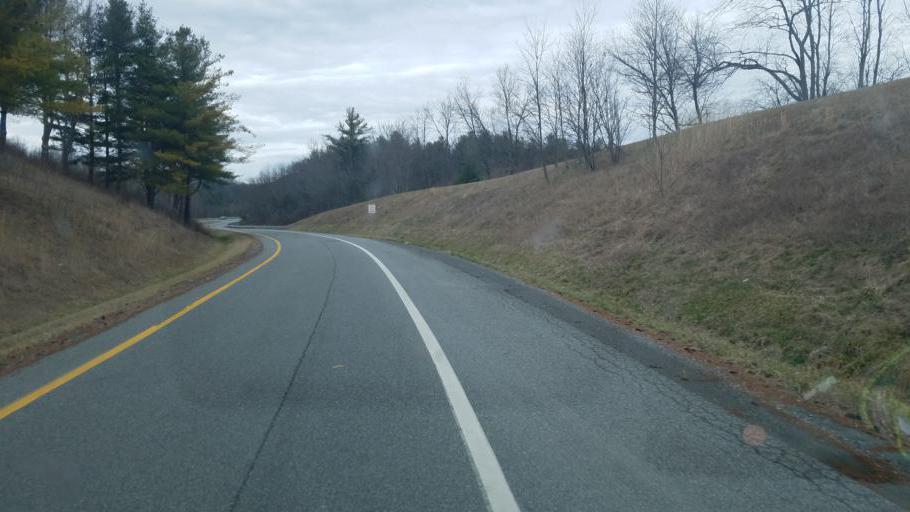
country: US
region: Virginia
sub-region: Bland County
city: Bland
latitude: 37.1018
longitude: -81.1273
